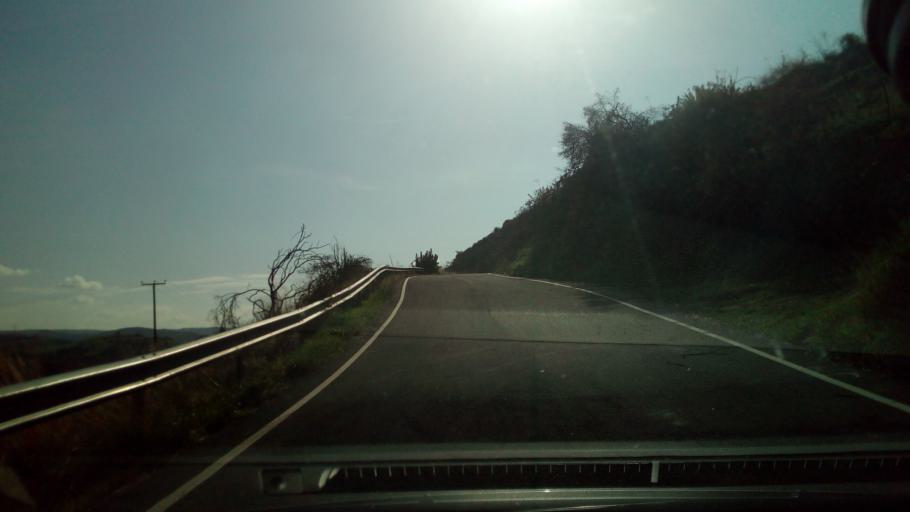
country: CY
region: Pafos
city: Polis
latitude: 34.9729
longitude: 32.4501
